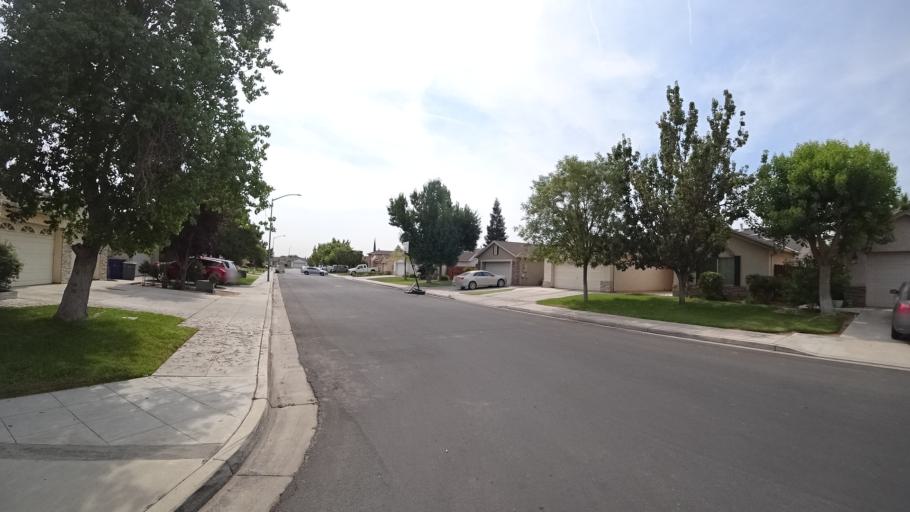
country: US
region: California
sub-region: Fresno County
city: West Park
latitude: 36.7620
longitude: -119.8924
